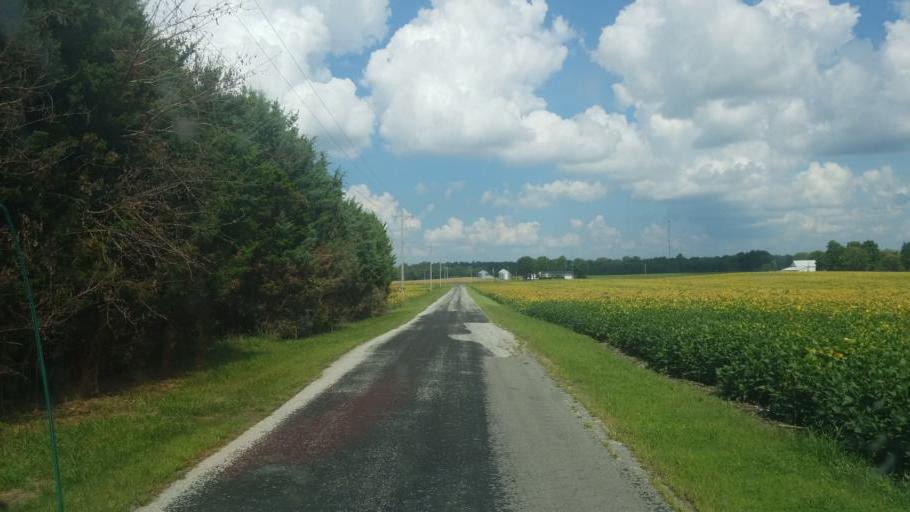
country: US
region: Ohio
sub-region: Hardin County
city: Kenton
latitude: 40.6999
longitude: -83.6386
